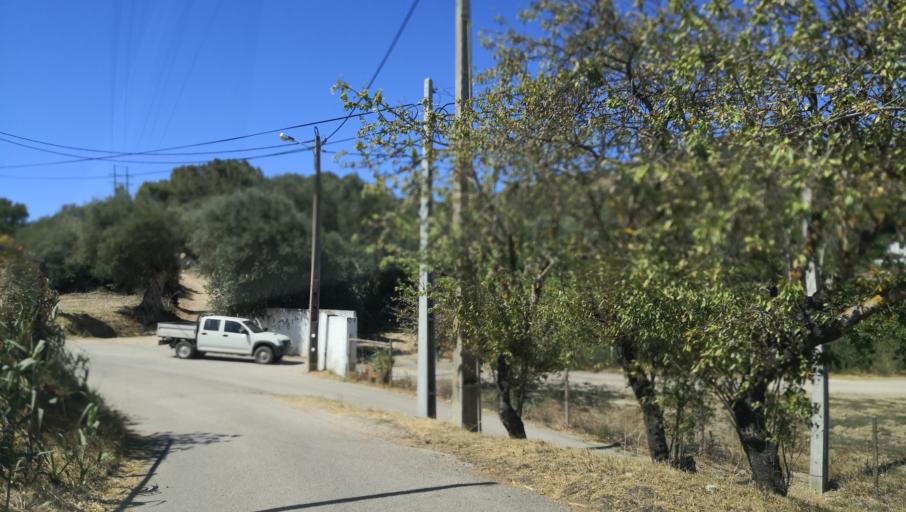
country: PT
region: Setubal
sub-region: Setubal
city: Setubal
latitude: 38.5362
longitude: -8.9148
